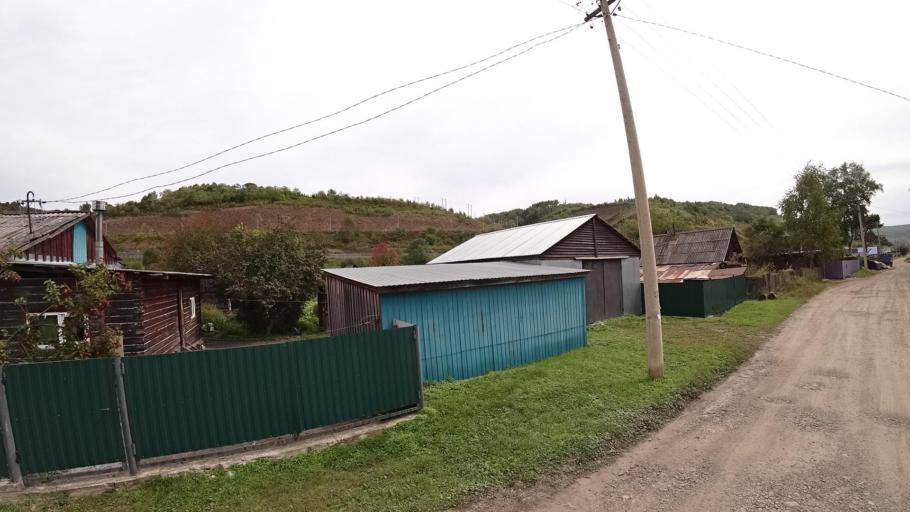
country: RU
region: Jewish Autonomous Oblast
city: Khingansk
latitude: 48.9980
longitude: 131.0546
